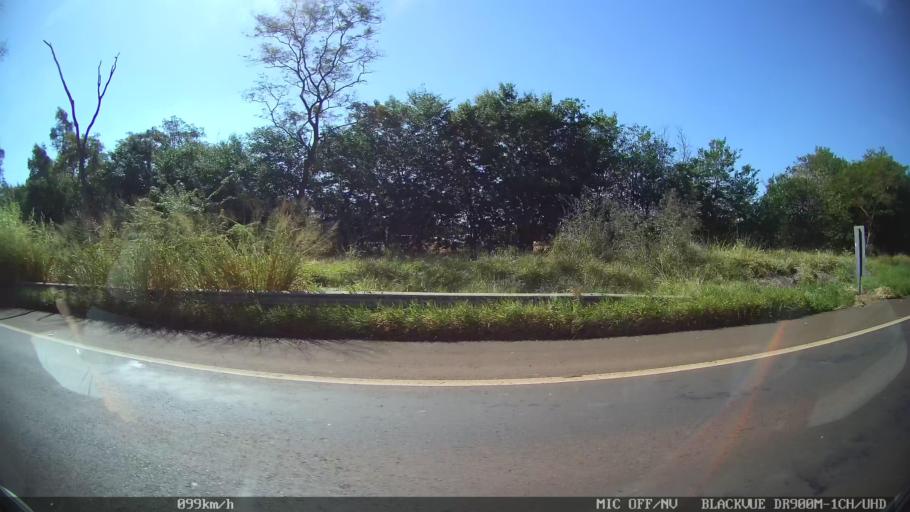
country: BR
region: Sao Paulo
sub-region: Franca
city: Franca
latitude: -20.5523
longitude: -47.4517
